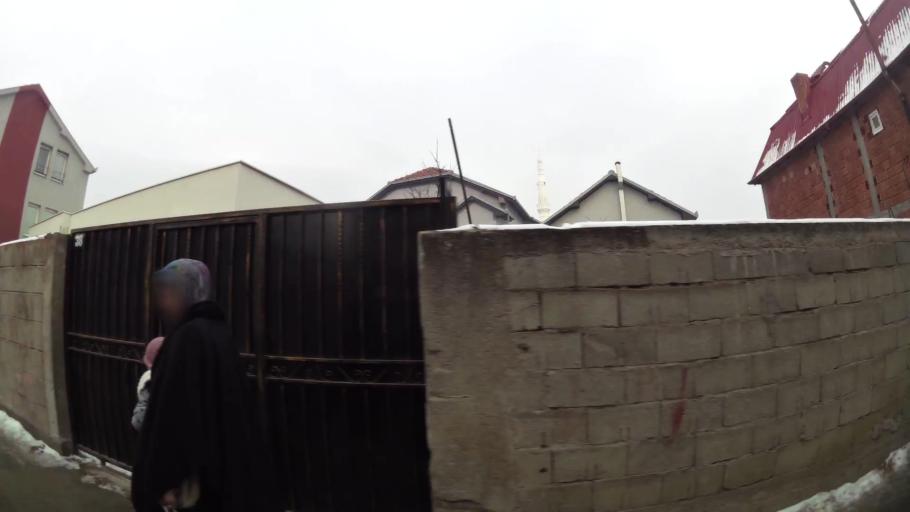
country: MK
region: Suto Orizari
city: Suto Orizare
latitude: 42.0282
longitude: 21.4249
